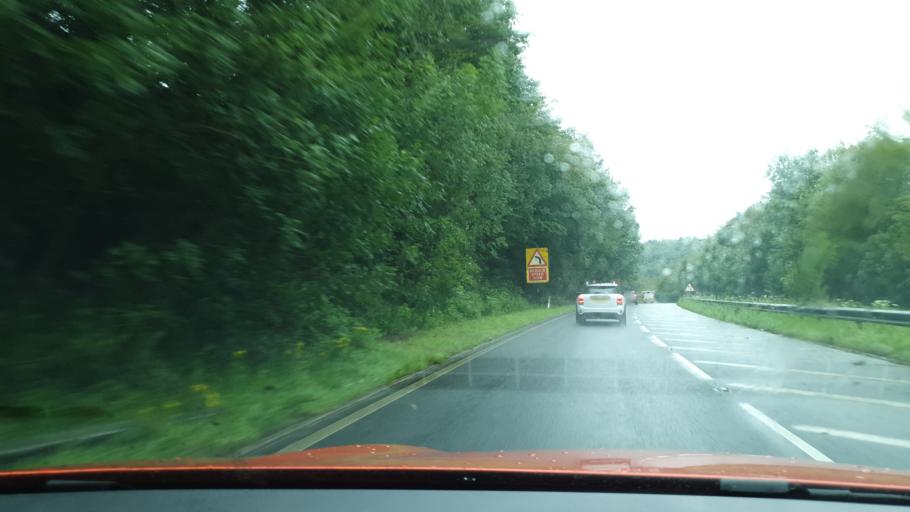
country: GB
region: England
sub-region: Cumbria
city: Grange-over-Sands
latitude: 54.2639
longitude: -2.9824
